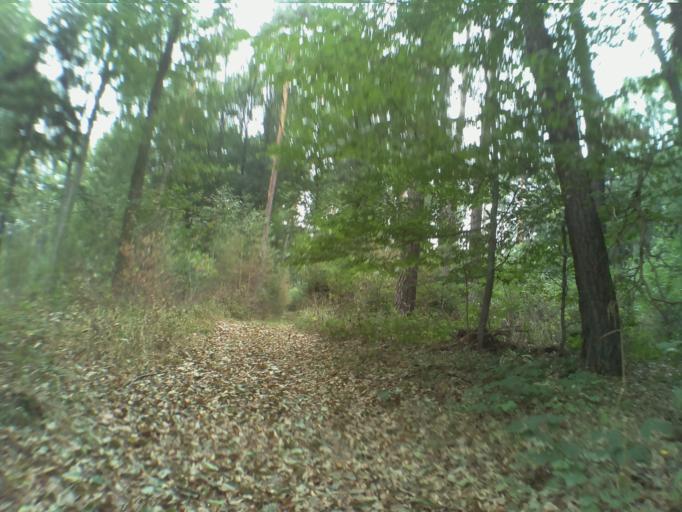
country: PL
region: Lower Silesian Voivodeship
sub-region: Powiat swidnicki
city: Strzegom
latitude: 50.9888
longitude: 16.3102
